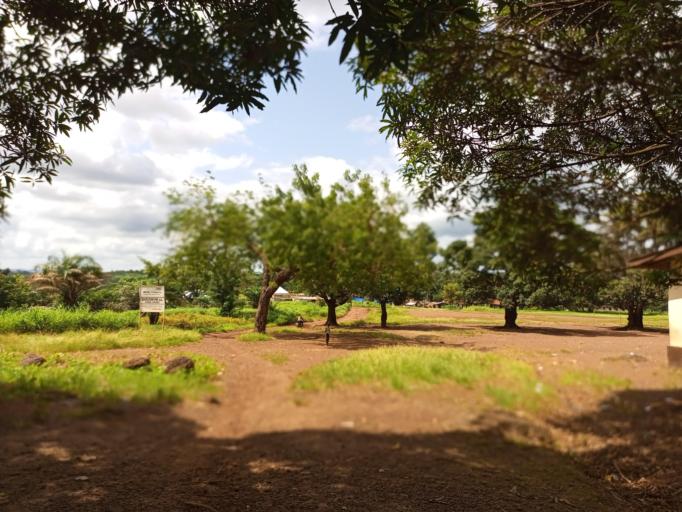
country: SL
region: Northern Province
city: Kamakwie
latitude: 9.5000
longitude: -12.2367
